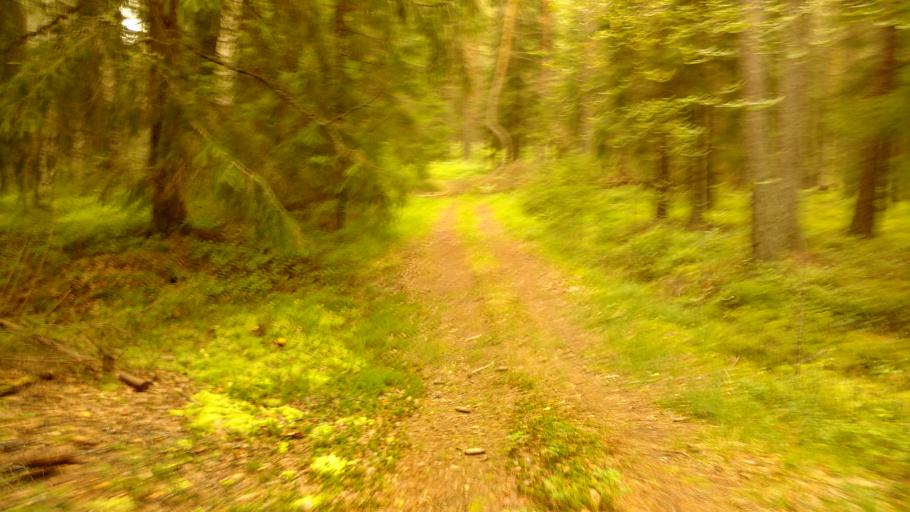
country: FI
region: Varsinais-Suomi
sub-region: Salo
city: Pertteli
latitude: 60.4009
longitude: 23.2221
